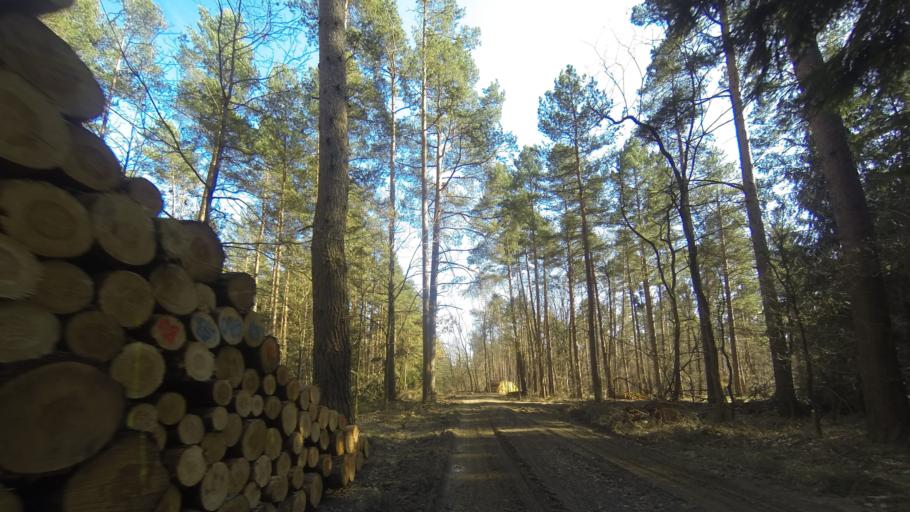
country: DE
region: Saxony
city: Laussnitz
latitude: 51.2611
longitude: 13.8528
